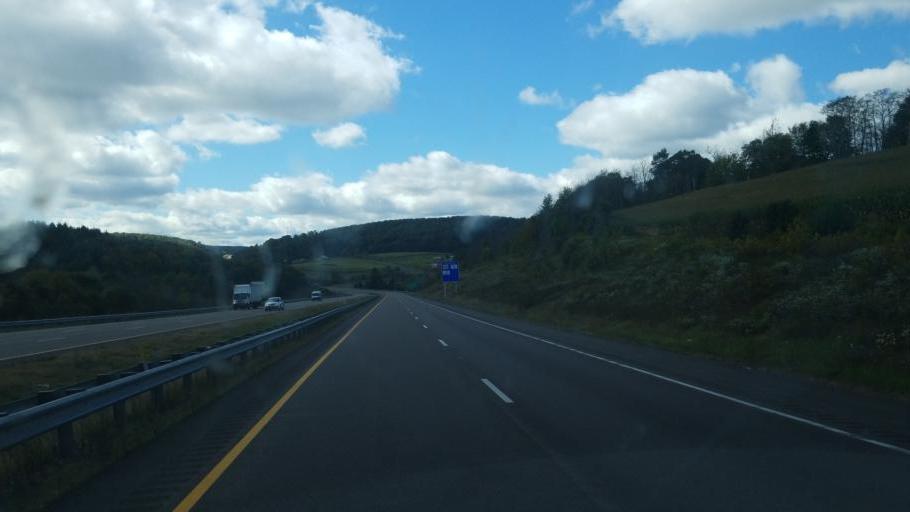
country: US
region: Maryland
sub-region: Allegany County
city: Frostburg
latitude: 39.6819
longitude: -79.0470
